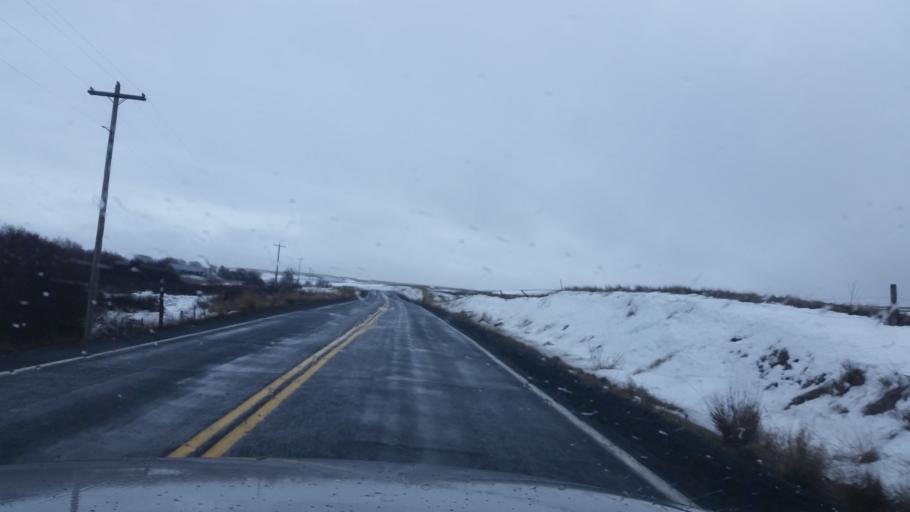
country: US
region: Washington
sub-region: Lincoln County
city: Davenport
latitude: 47.3508
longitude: -118.0982
